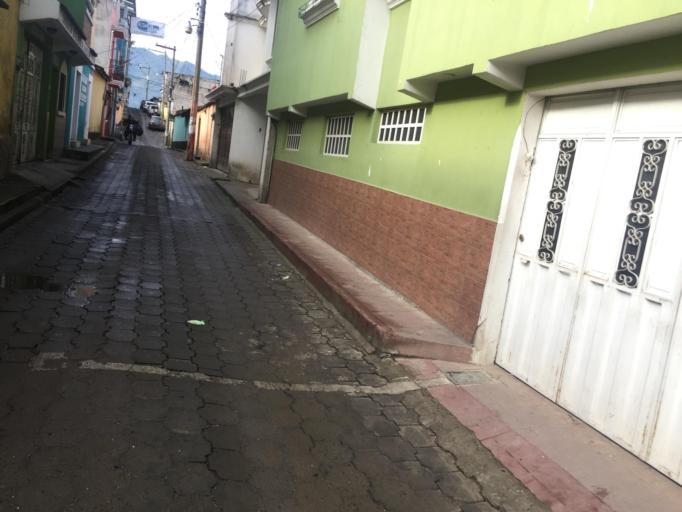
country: GT
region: Totonicapan
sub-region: Municipio de Totonicapan
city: Totonicapan
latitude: 14.9122
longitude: -91.3575
